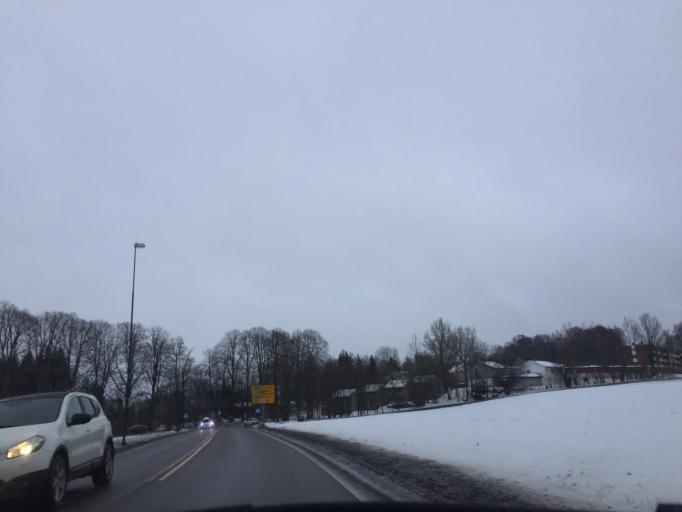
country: NO
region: Akershus
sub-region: Frogn
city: Drobak
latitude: 59.6879
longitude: 10.6618
